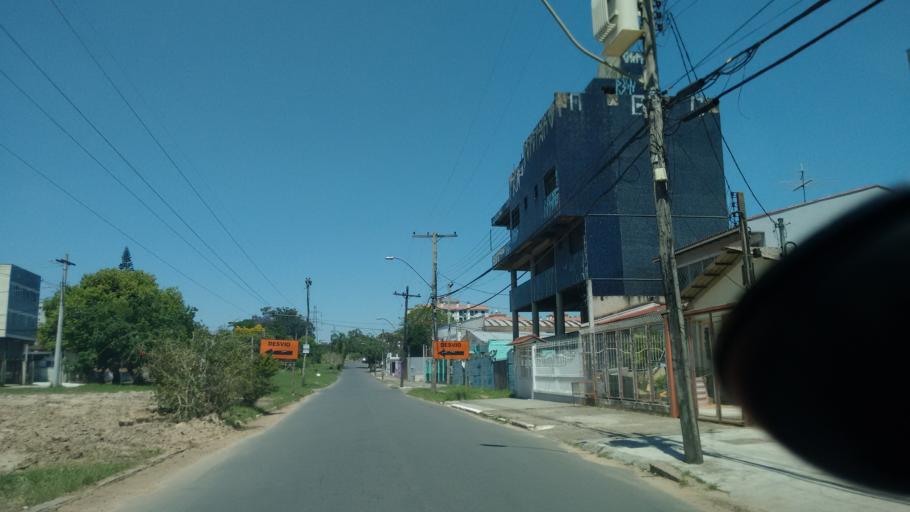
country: BR
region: Rio Grande do Sul
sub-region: Cachoeirinha
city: Cachoeirinha
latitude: -29.9990
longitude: -51.1263
